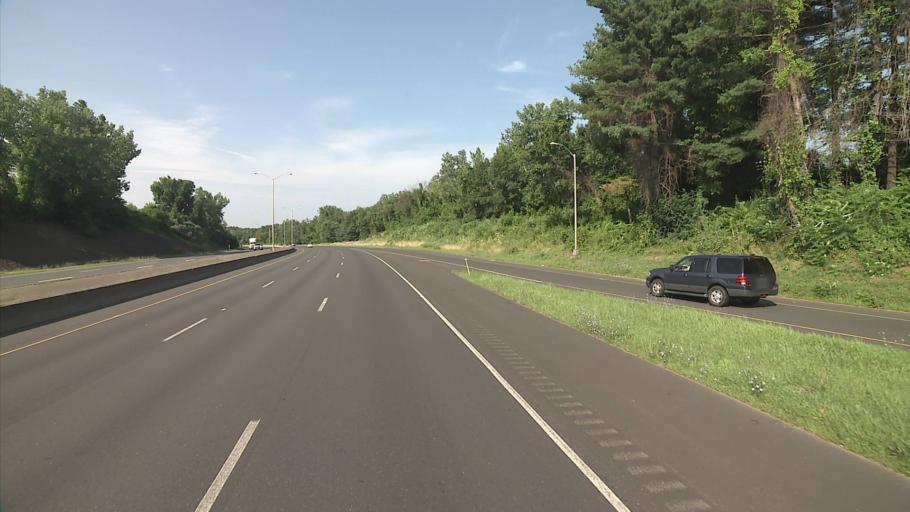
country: US
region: Connecticut
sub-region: Hartford County
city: Enfield
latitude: 41.9525
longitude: -72.6024
